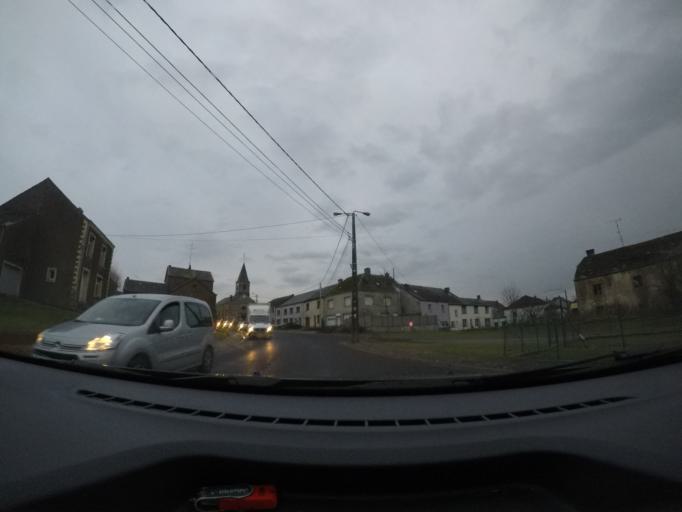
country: BE
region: Wallonia
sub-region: Province du Luxembourg
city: Tintigny
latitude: 49.6664
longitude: 5.4957
